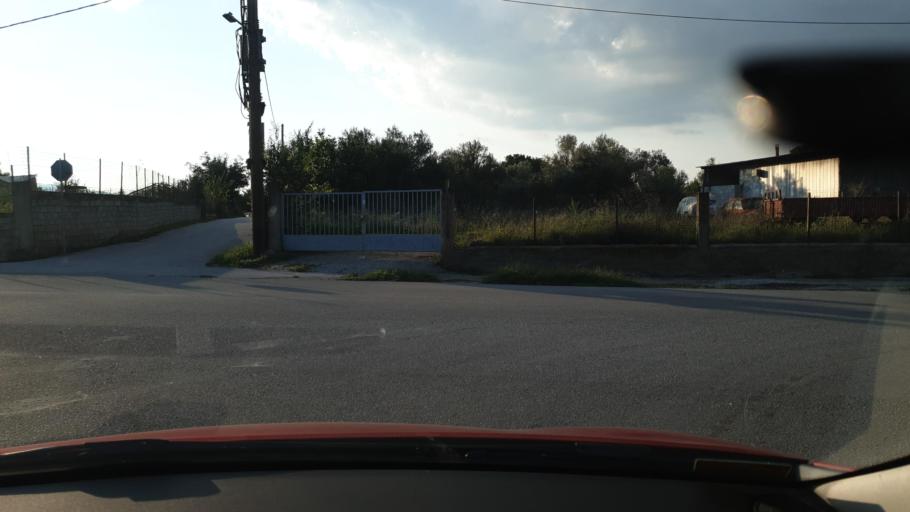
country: GR
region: Central Macedonia
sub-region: Nomos Chalkidikis
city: Galatista
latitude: 40.5567
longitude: 23.3045
